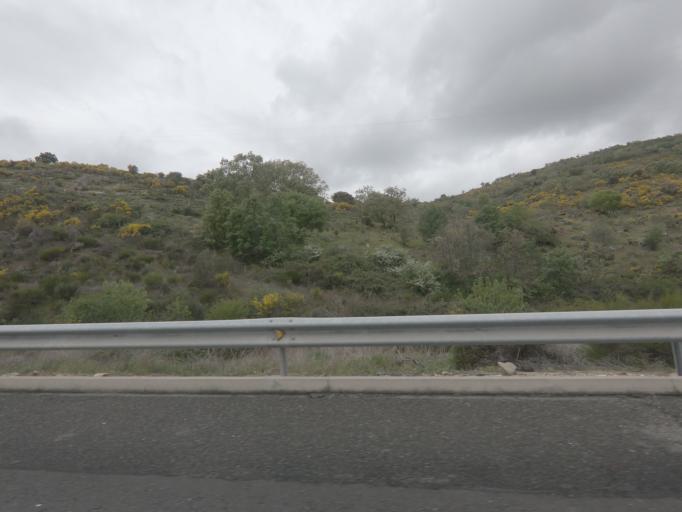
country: ES
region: Extremadura
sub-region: Provincia de Caceres
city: Hervas
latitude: 40.2839
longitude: -5.9004
